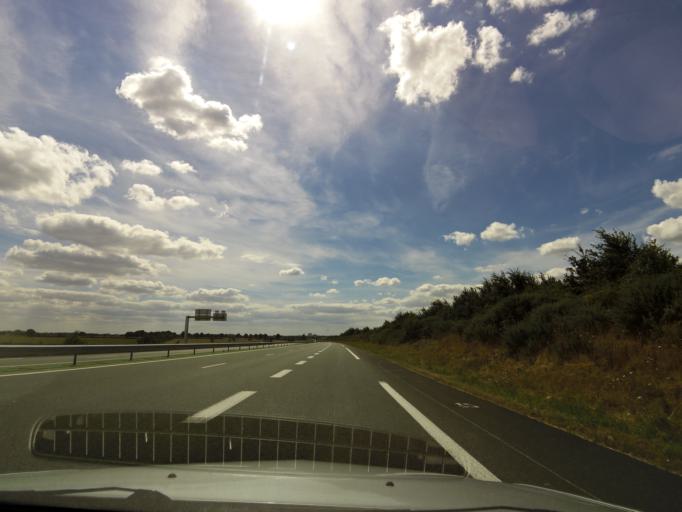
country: FR
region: Pays de la Loire
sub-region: Departement de la Vendee
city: Les Essarts
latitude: 46.8059
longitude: -1.2132
